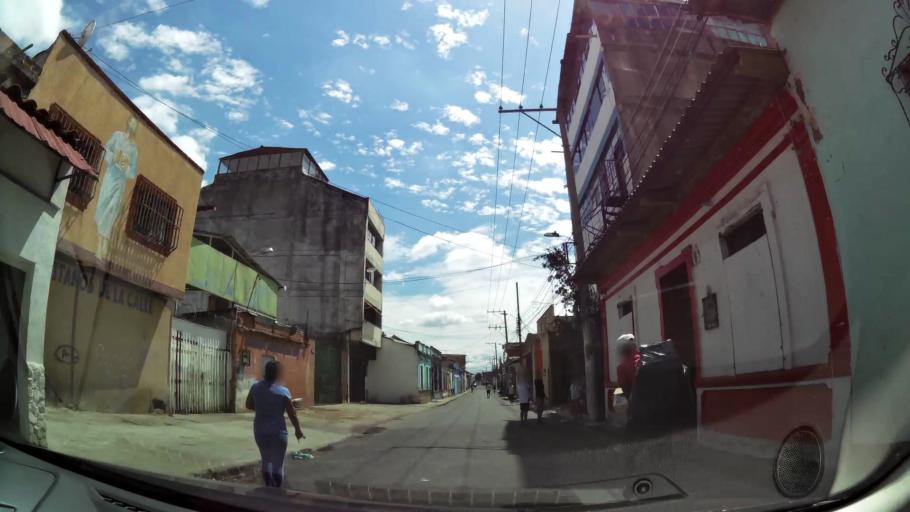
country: CO
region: Valle del Cauca
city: Cali
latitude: 3.4444
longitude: -76.5318
